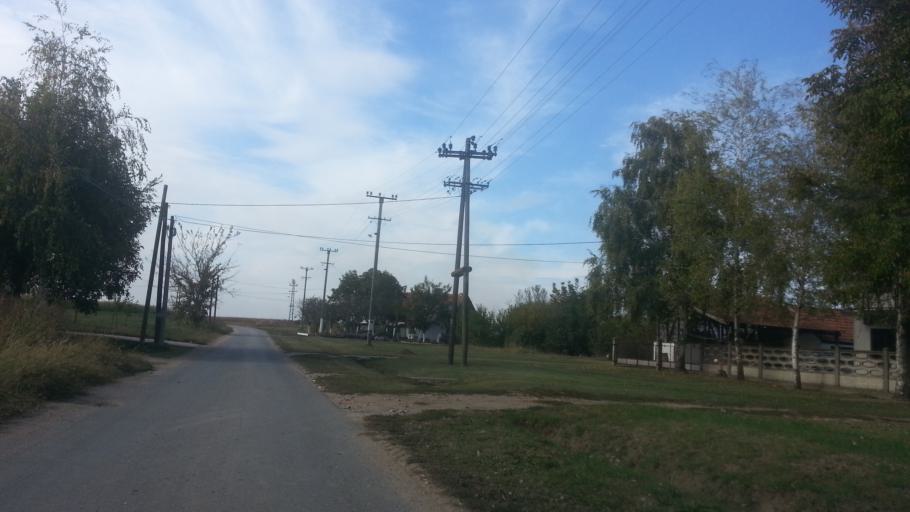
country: RS
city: Belegis
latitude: 45.0227
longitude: 20.3137
